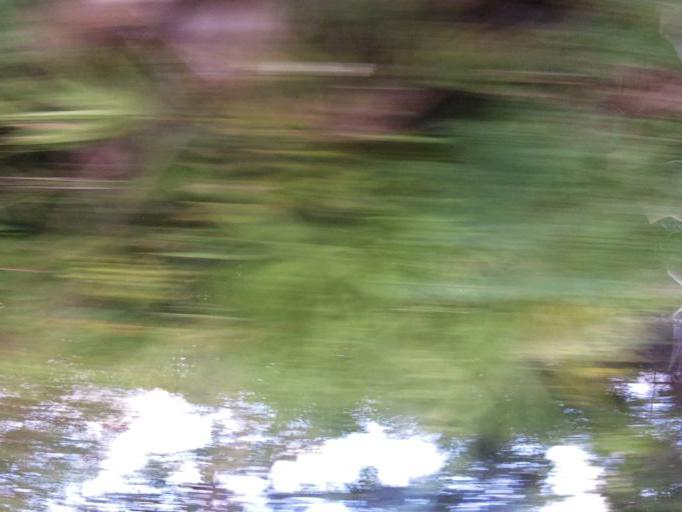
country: US
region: Florida
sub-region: Saint Johns County
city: Fruit Cove
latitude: 30.1806
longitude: -81.6303
